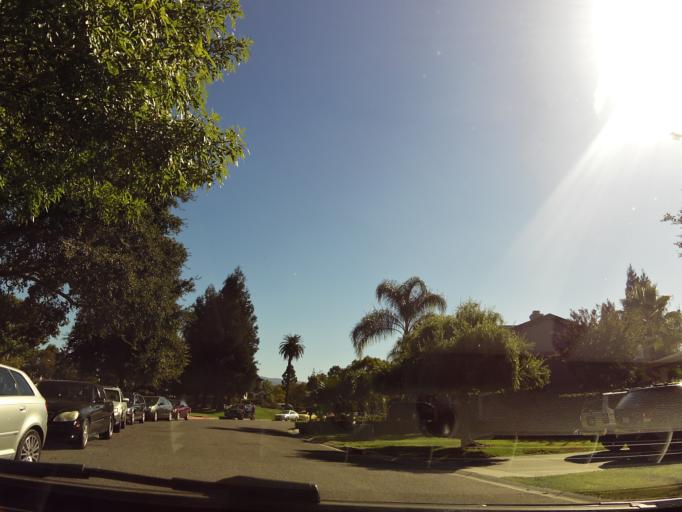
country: US
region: California
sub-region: Santa Clara County
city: Monte Sereno
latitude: 37.2664
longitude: -121.9768
